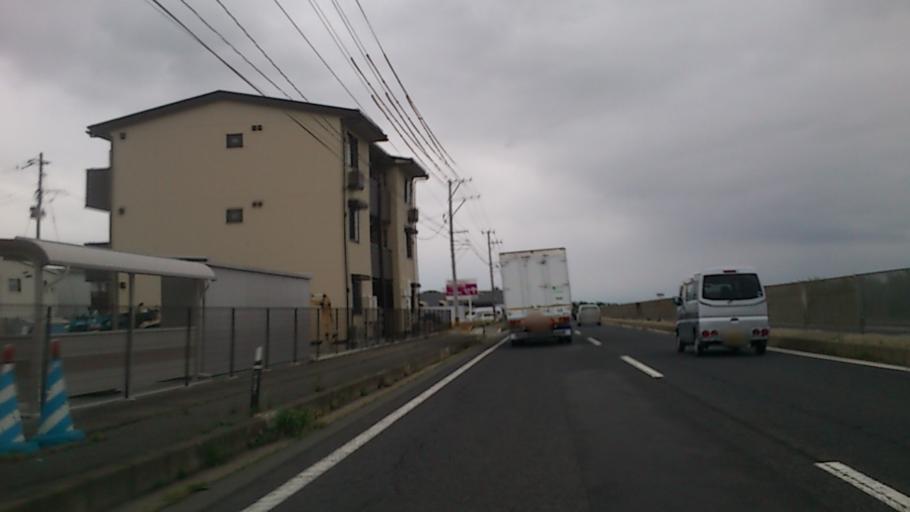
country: JP
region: Yamagata
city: Higashine
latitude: 38.4118
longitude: 140.3744
